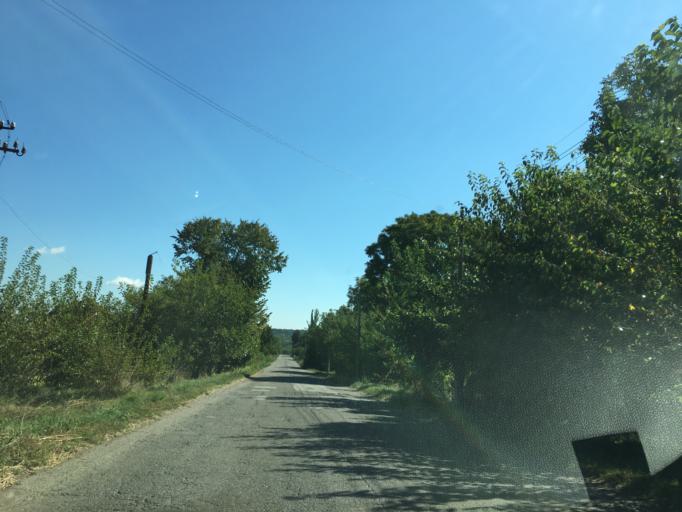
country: RO
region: Dolj
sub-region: Comuna Desa
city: Desa
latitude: 43.7671
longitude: 23.0100
